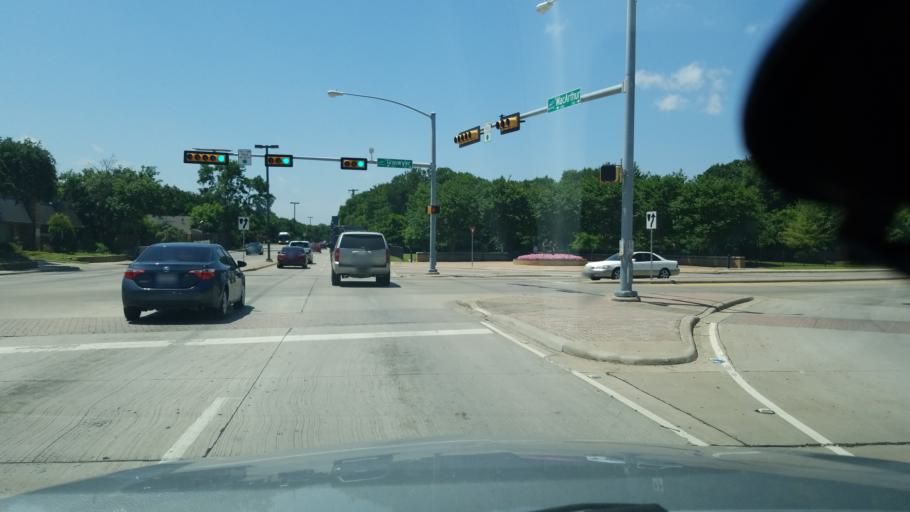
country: US
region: Texas
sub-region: Dallas County
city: Irving
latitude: 32.8293
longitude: -96.9593
